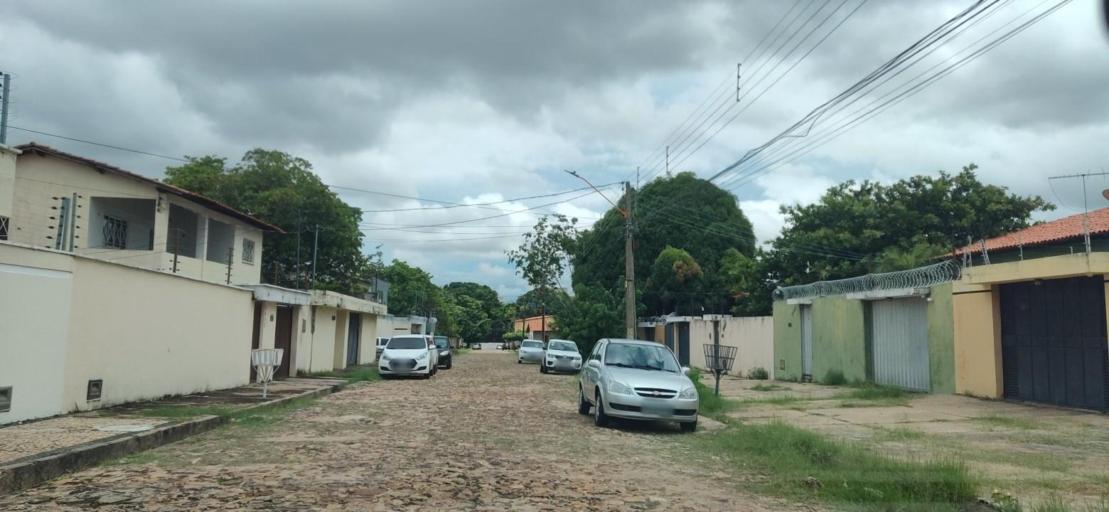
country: BR
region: Piaui
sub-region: Teresina
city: Teresina
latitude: -5.0753
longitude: -42.7636
